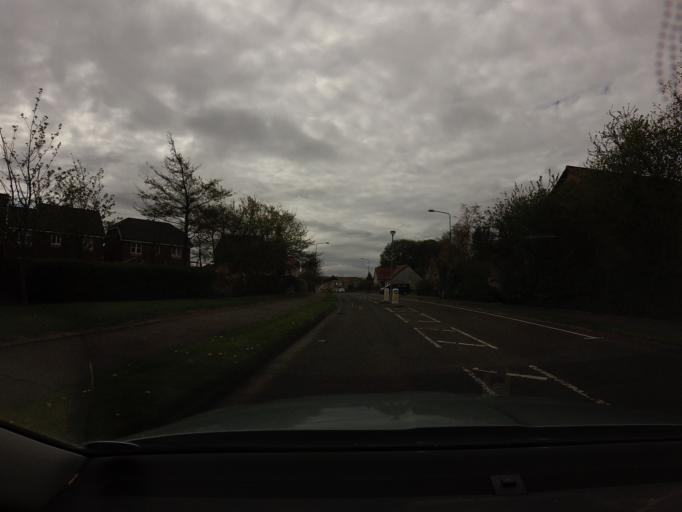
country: GB
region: Scotland
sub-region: West Lothian
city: Broxburn
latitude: 55.9363
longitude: -3.4815
